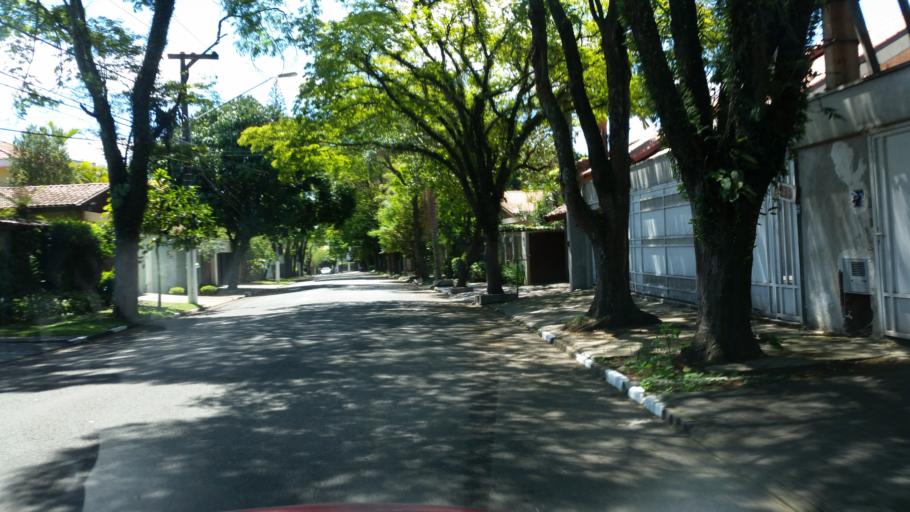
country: BR
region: Sao Paulo
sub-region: Diadema
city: Diadema
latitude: -23.6407
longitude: -46.6854
